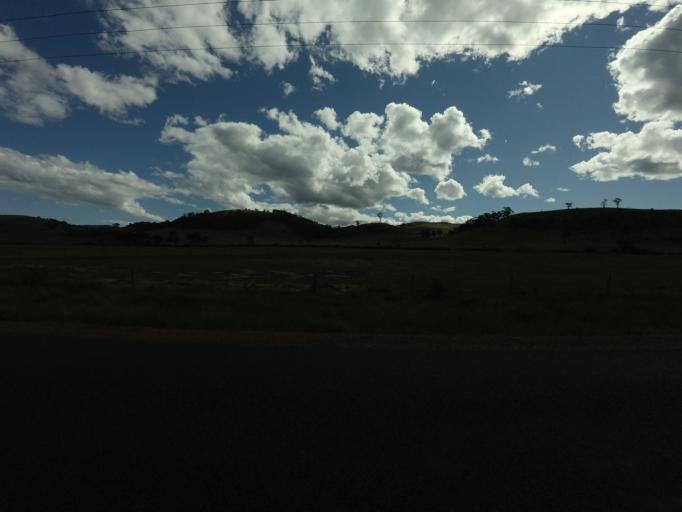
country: AU
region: Tasmania
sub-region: Brighton
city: Bridgewater
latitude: -42.5246
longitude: 147.3577
